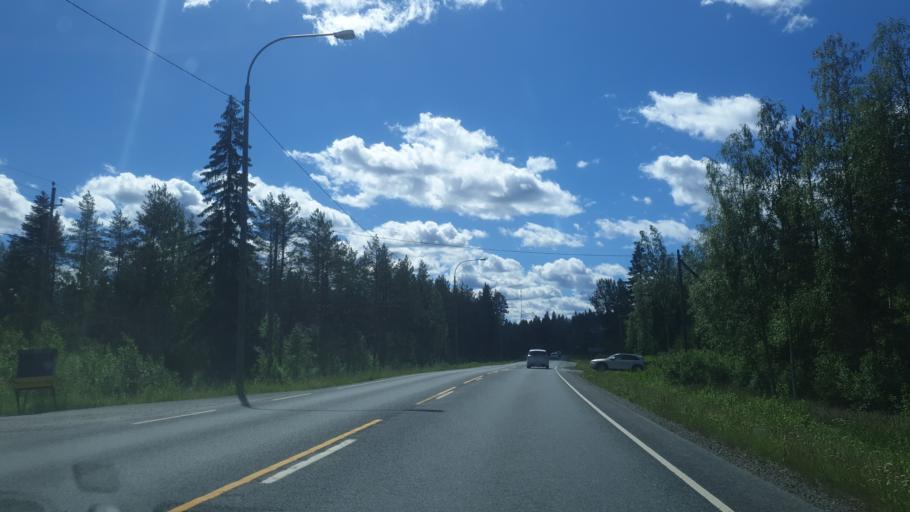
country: FI
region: Northern Savo
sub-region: Varkaus
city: Leppaevirta
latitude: 62.5610
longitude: 27.6212
